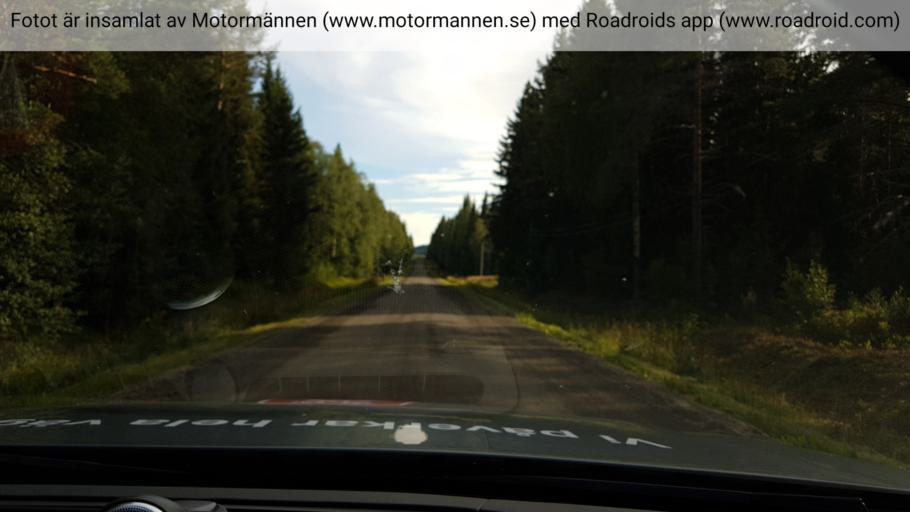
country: SE
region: Jaemtland
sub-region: Stroemsunds Kommun
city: Stroemsund
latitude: 64.0651
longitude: 15.8198
